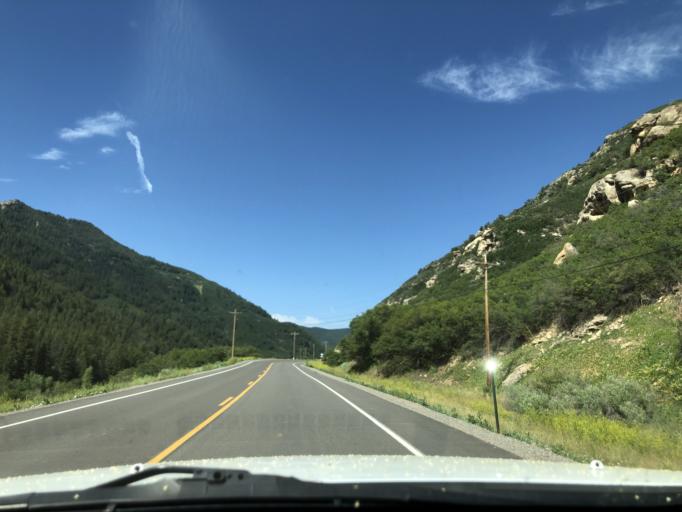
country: US
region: Colorado
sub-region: Delta County
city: Paonia
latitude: 38.9366
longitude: -107.3903
